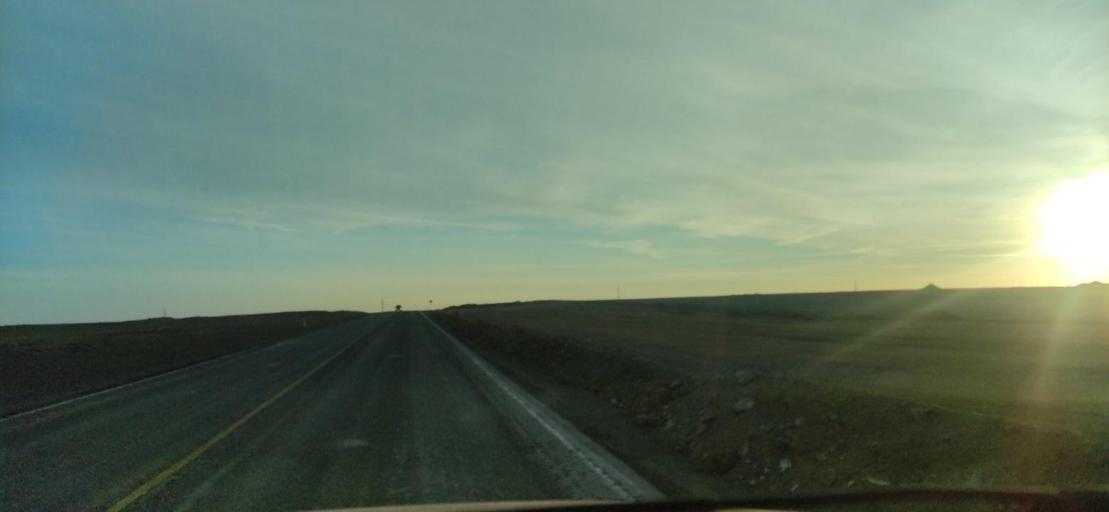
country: KZ
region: Qaraghandy
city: Saryshaghan
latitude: 46.0701
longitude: 73.6017
